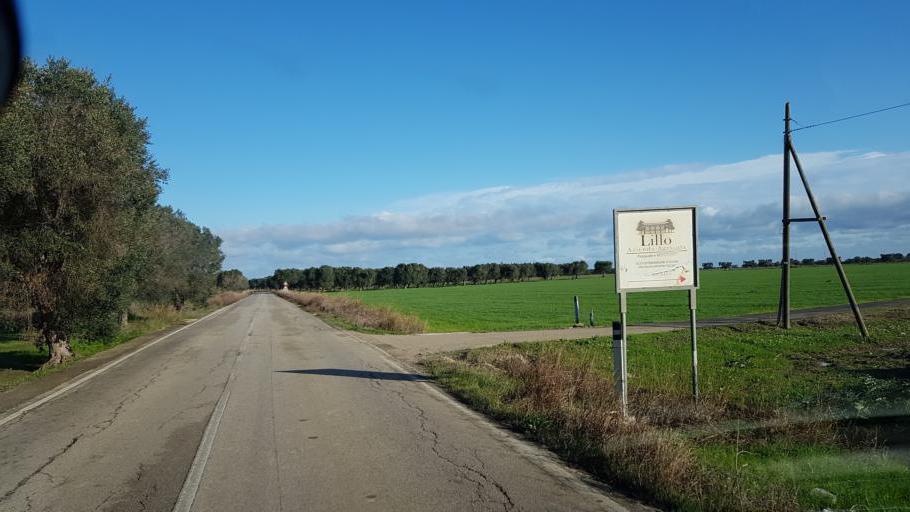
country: IT
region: Apulia
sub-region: Provincia di Brindisi
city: Tuturano
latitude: 40.5610
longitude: 17.9482
